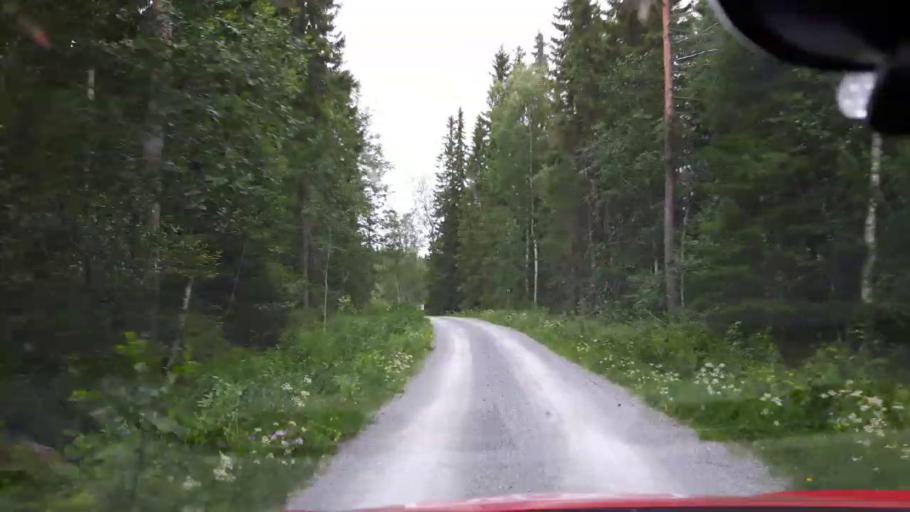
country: SE
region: Jaemtland
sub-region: OEstersunds Kommun
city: Brunflo
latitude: 63.0342
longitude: 14.9291
